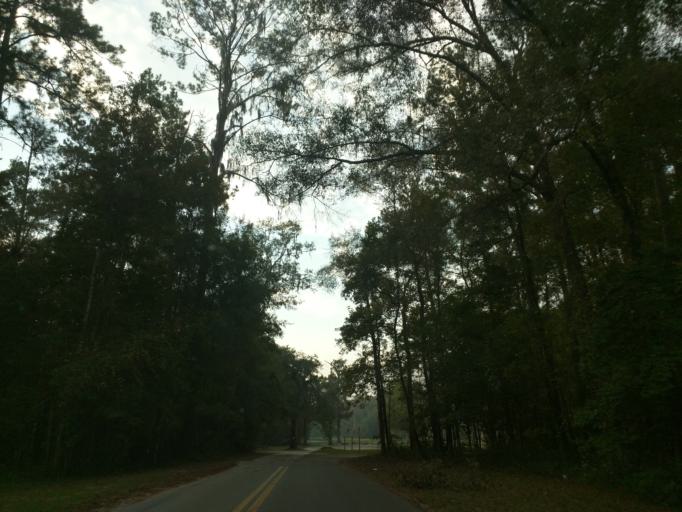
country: US
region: Florida
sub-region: Jefferson County
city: Monticello
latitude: 30.3416
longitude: -83.9909
